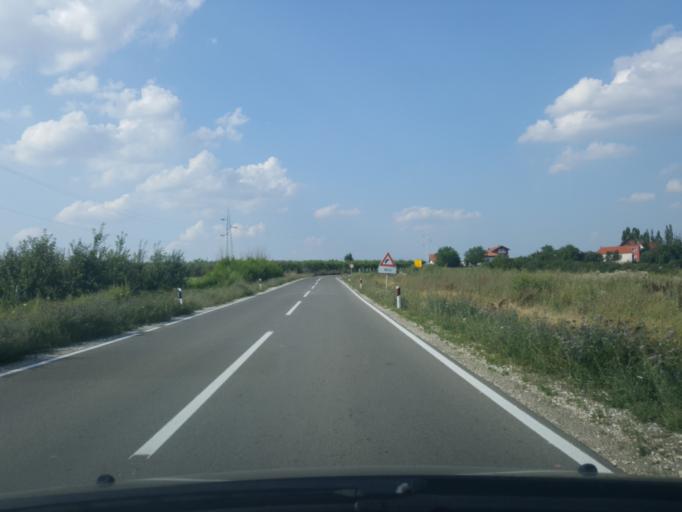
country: RS
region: Central Serbia
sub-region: Sumadijski Okrug
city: Topola
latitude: 44.2167
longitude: 20.6189
